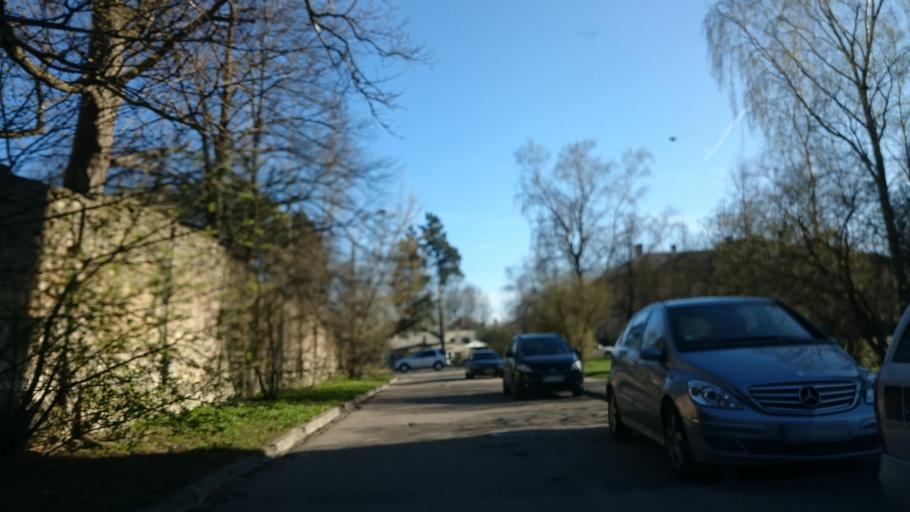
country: LV
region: Riga
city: Bergi
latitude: 56.9934
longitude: 24.2309
